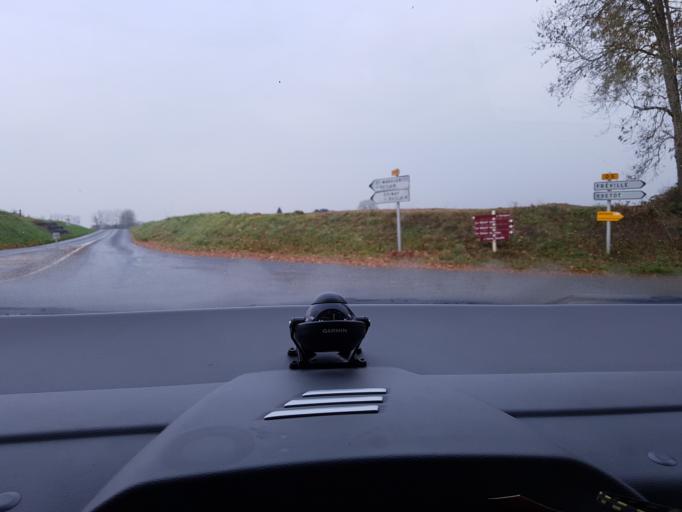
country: FR
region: Haute-Normandie
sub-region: Departement de la Seine-Maritime
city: Saint-Paer
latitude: 49.5148
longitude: 0.8615
